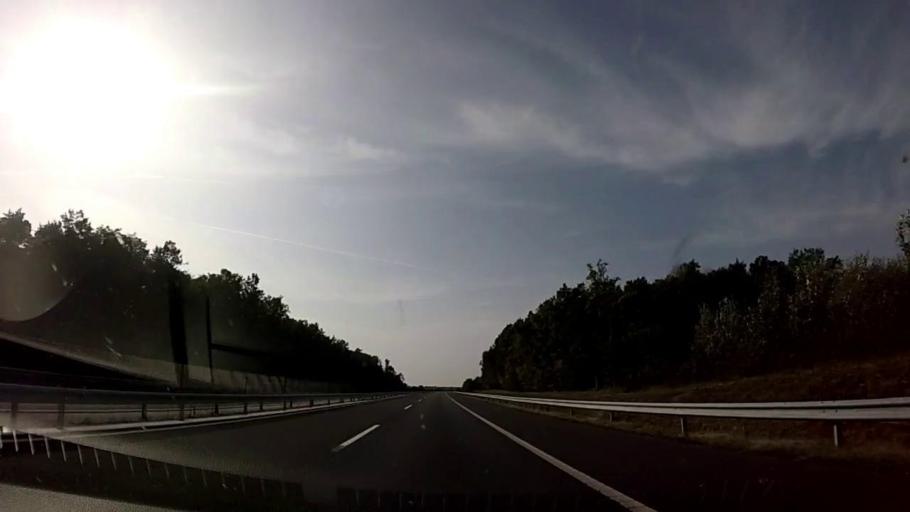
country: HU
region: Somogy
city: Balatonbereny
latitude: 46.6346
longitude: 17.2821
